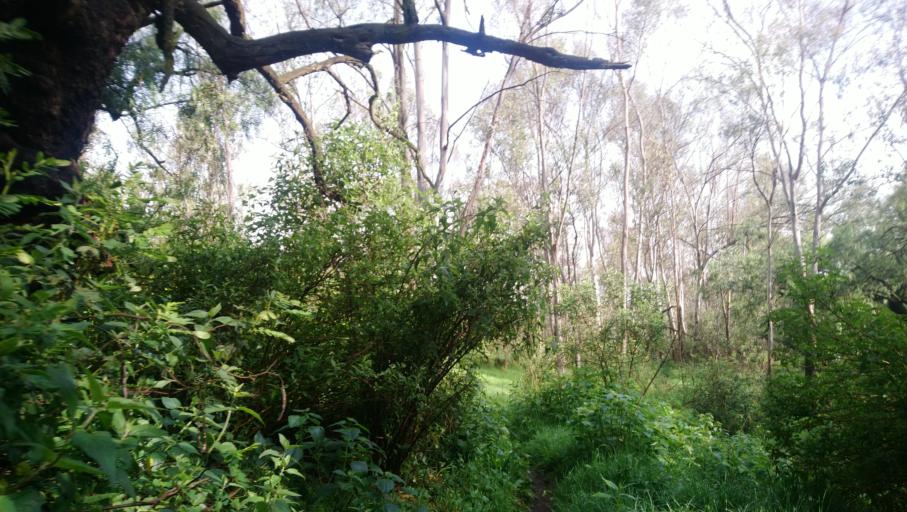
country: MX
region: Mexico
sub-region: Tultitlan
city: Ampliacion San Mateo (Colonia Solidaridad)
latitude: 19.6077
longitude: -99.1232
